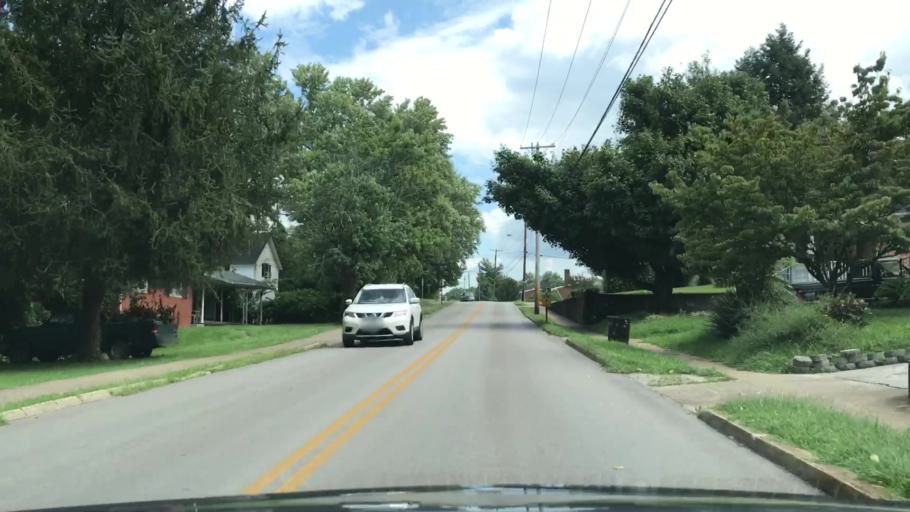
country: US
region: Kentucky
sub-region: Pulaski County
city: Somerset
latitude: 37.0814
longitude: -84.6042
